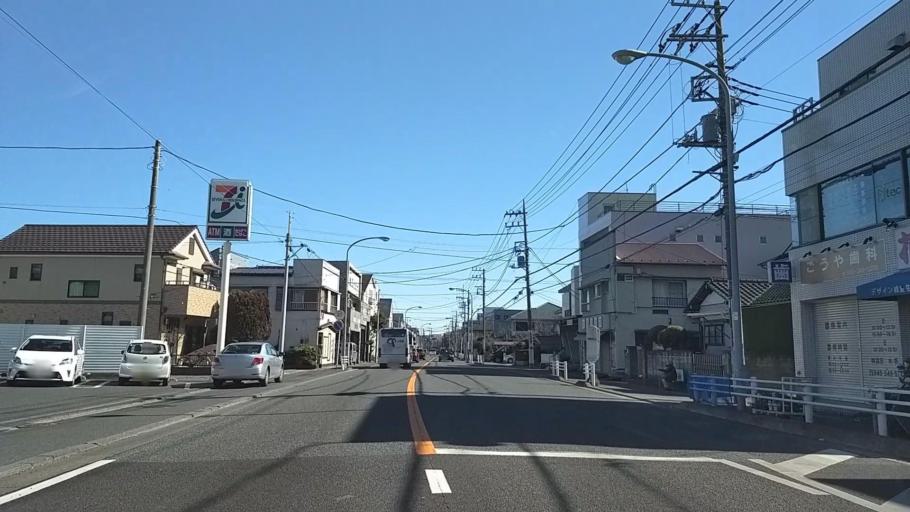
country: JP
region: Kanagawa
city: Zushi
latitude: 35.3285
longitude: 139.6076
